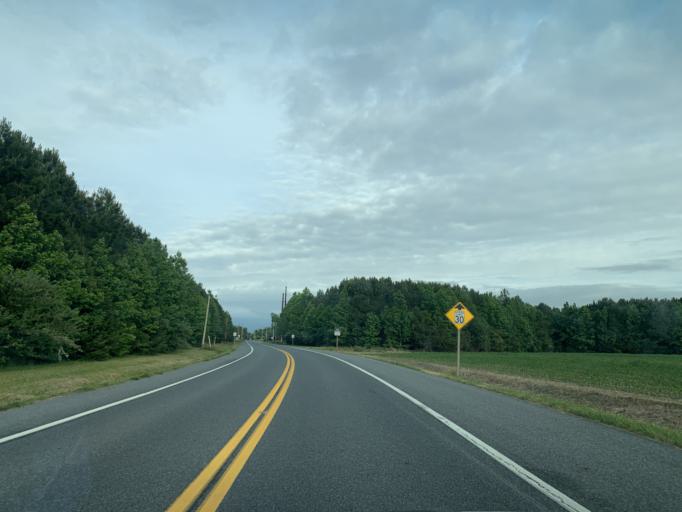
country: US
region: Virginia
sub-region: Accomack County
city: Captains Cove
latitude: 38.0583
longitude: -75.4211
